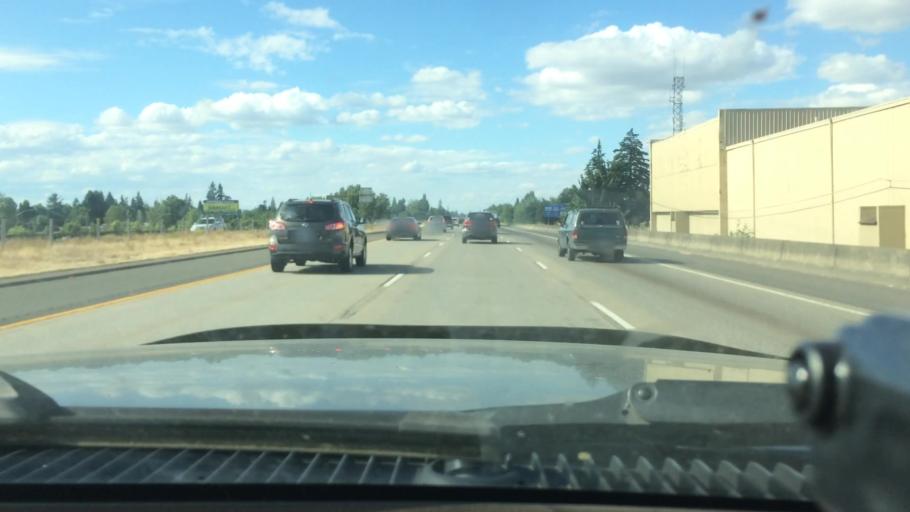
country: US
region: Oregon
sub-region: Marion County
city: Four Corners
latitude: 44.9294
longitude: -122.9902
